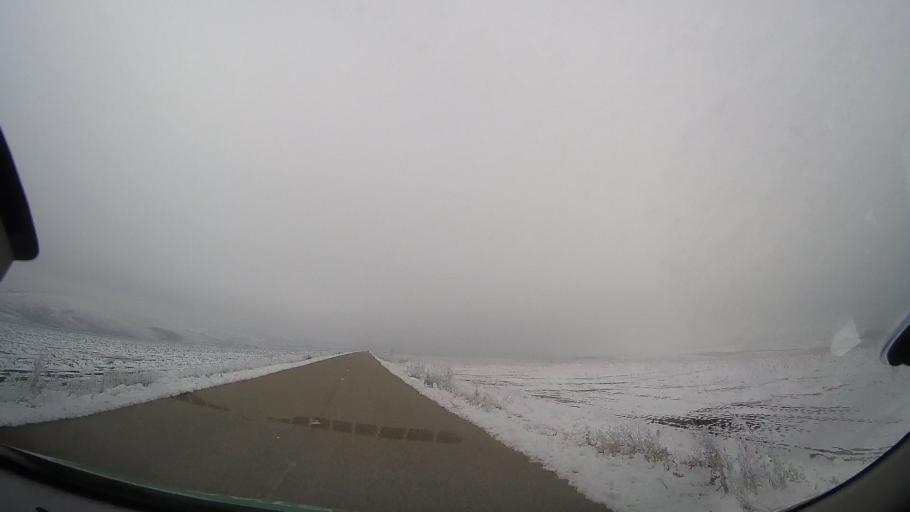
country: RO
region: Vaslui
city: Coroiesti
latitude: 46.2174
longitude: 27.4800
